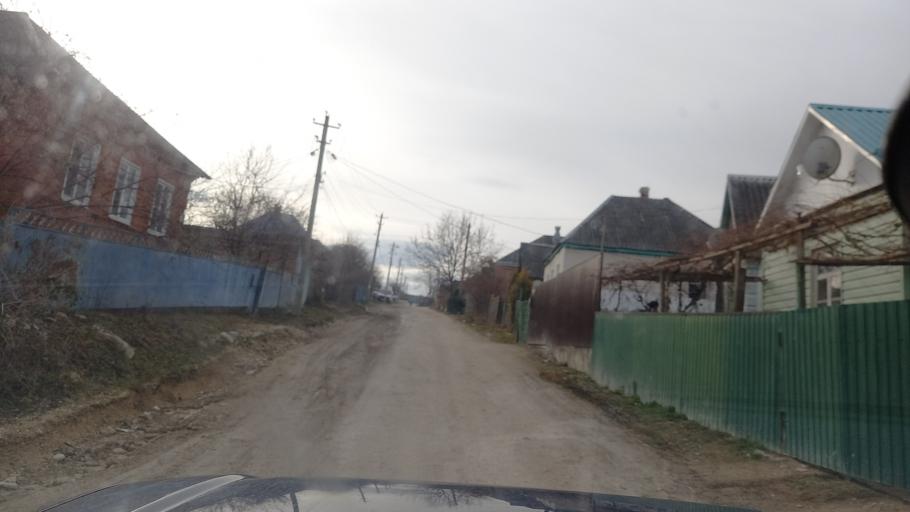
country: RU
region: Adygeya
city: Kamennomostskiy
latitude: 44.2942
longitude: 40.1907
